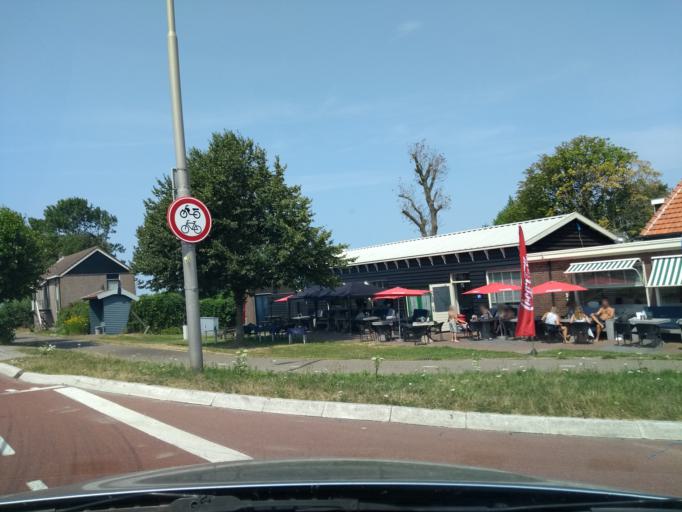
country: NL
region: North Holland
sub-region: Gemeente Heerhugowaard
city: Heerhugowaard
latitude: 52.6326
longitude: 4.8315
